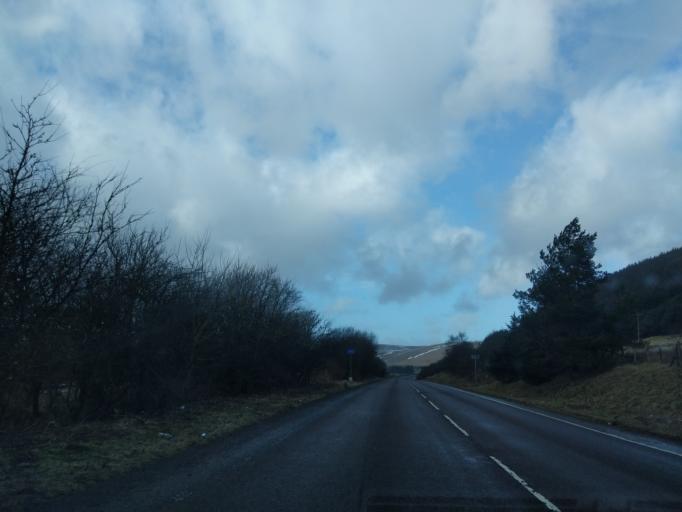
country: GB
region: Scotland
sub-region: Dumfries and Galloway
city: Moffat
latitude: 55.4302
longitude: -3.6330
